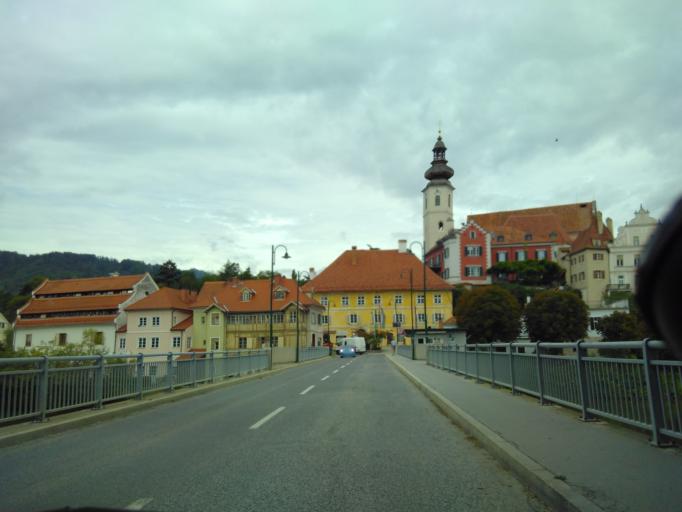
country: AT
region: Styria
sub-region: Politischer Bezirk Graz-Umgebung
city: Frohnleiten
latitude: 47.2686
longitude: 15.3250
